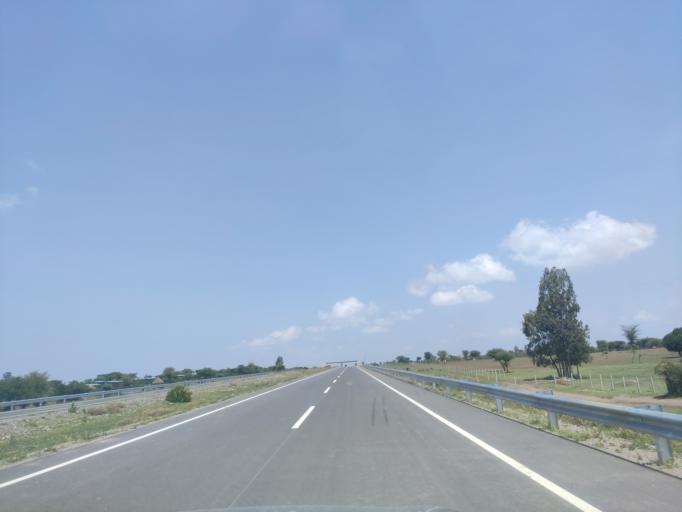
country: ET
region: Oromiya
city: Ziway
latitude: 8.2559
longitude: 38.8947
